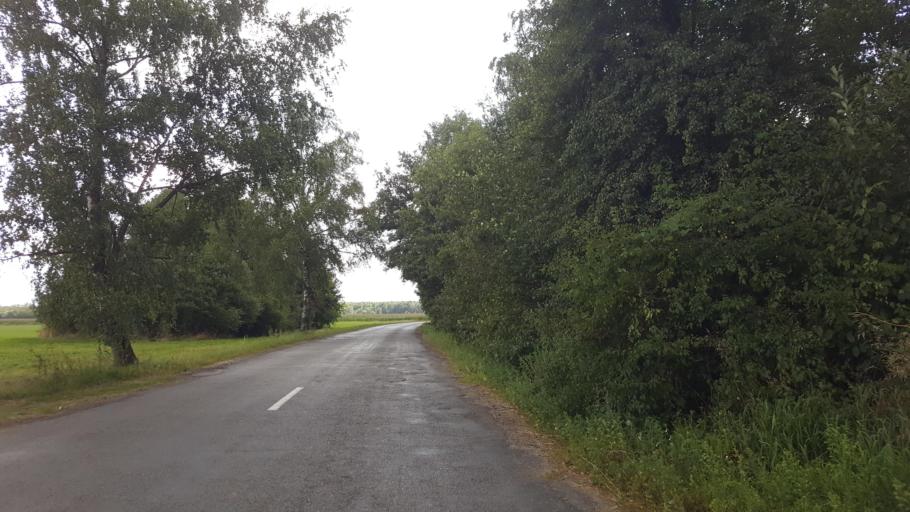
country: BY
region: Brest
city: Zhabinka
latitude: 52.2599
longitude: 23.9847
